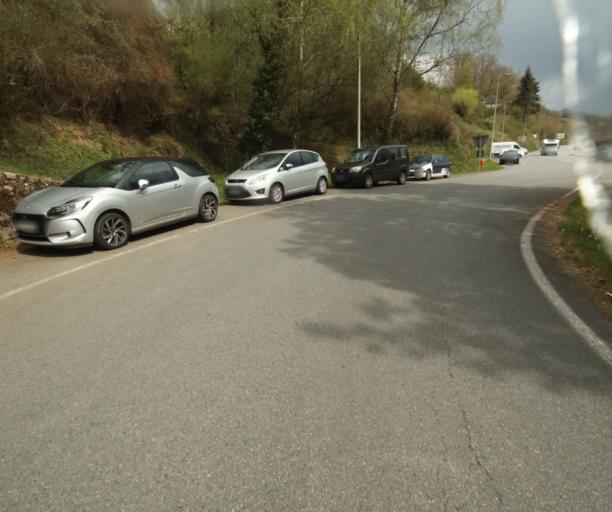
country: FR
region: Limousin
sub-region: Departement de la Correze
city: Tulle
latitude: 45.2529
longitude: 1.7545
